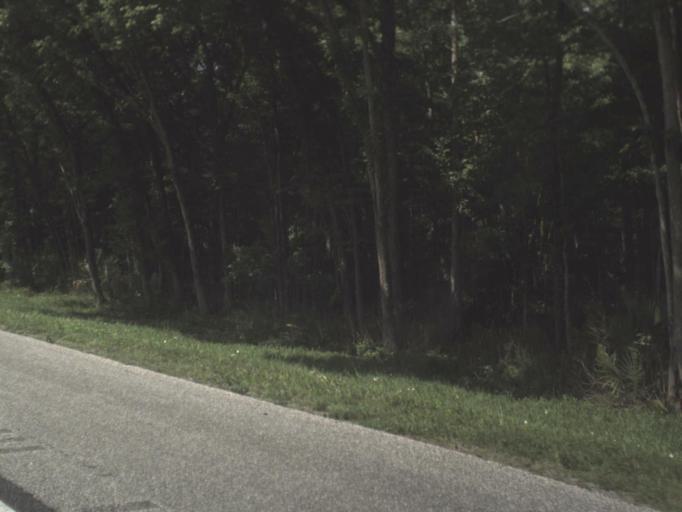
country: US
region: Florida
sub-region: Saint Johns County
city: Fruit Cove
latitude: 30.0269
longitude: -81.4862
